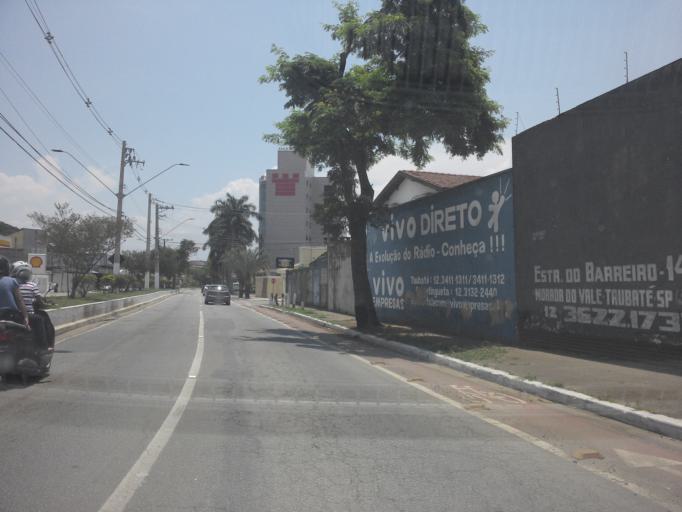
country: BR
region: Sao Paulo
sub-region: Taubate
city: Taubate
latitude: -23.0412
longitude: -45.5831
